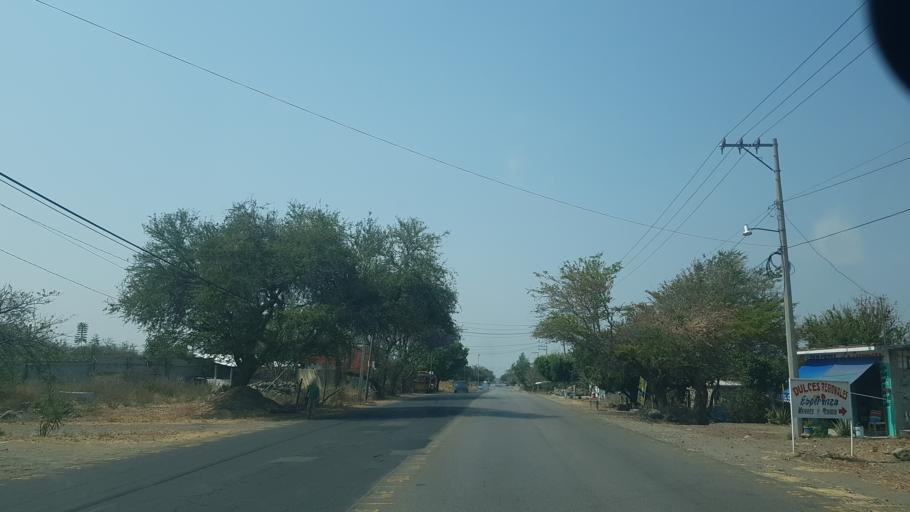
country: MX
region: Morelos
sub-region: Temoac
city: Huazulco
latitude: 18.7499
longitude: -98.7820
